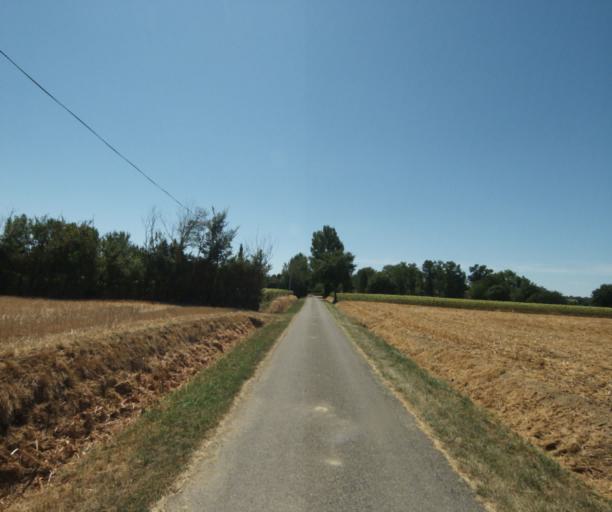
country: FR
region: Midi-Pyrenees
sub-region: Departement de la Haute-Garonne
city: Revel
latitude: 43.4804
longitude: 1.9472
